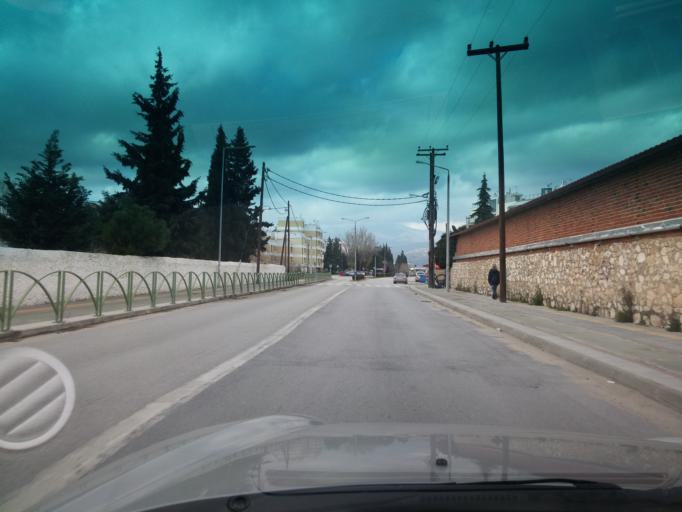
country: GR
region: East Macedonia and Thrace
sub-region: Nomos Rodopis
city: Komotini
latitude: 41.1234
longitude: 25.3962
